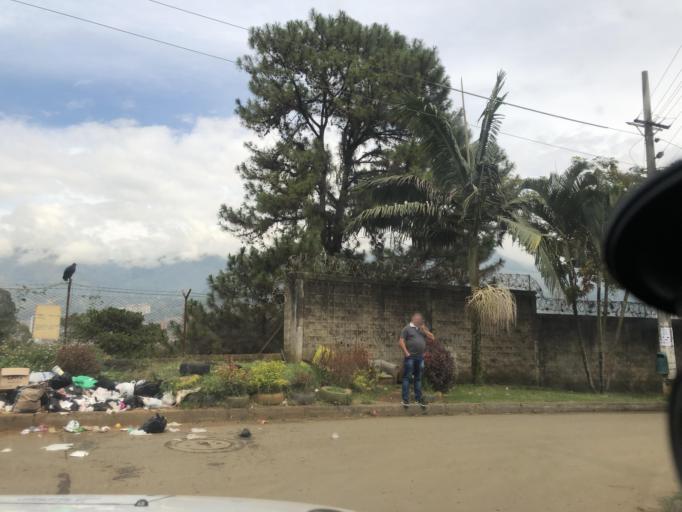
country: CO
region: Antioquia
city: Bello
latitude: 6.3279
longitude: -75.5437
